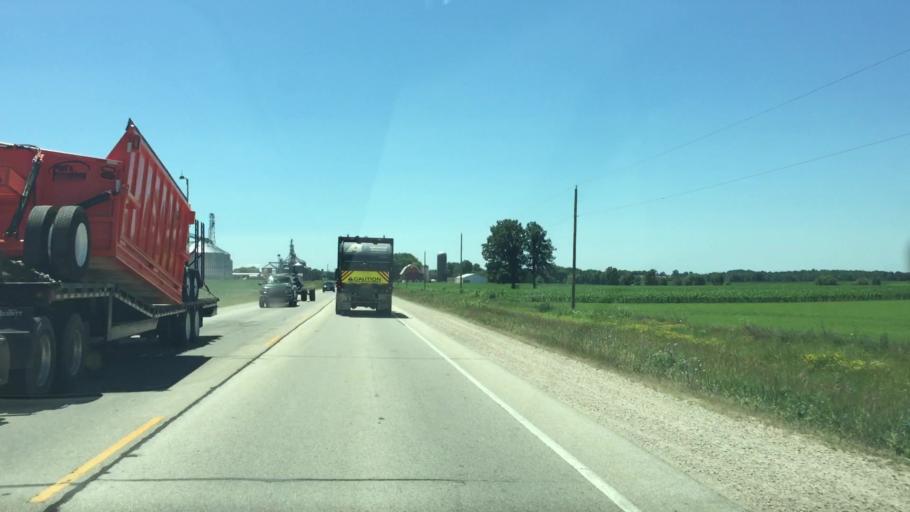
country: US
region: Wisconsin
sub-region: Calumet County
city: Chilton
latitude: 44.0820
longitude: -88.1635
